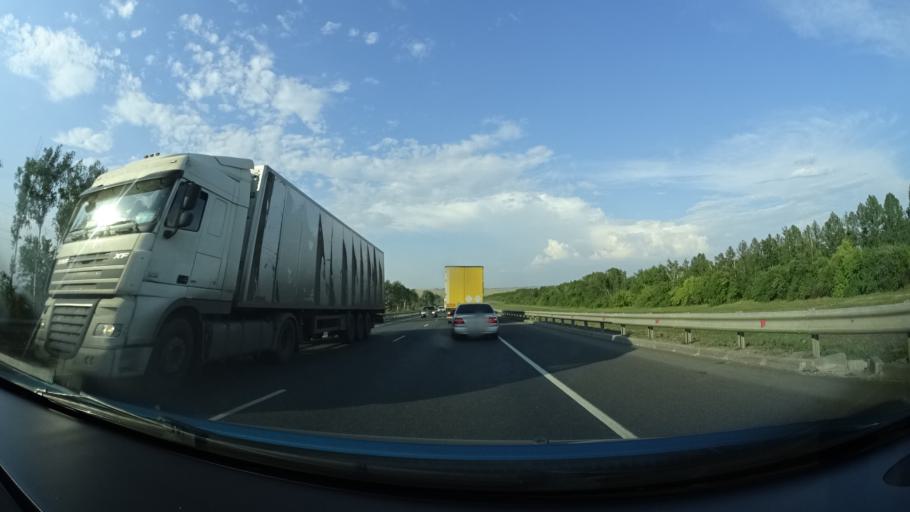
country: RU
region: Samara
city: Krasnyy Yar
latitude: 53.6778
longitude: 50.7755
